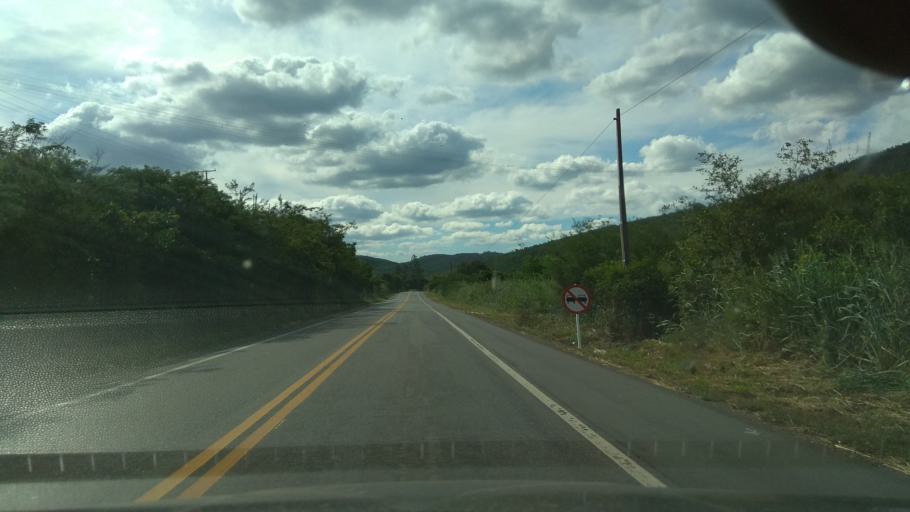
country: BR
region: Bahia
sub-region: Jequie
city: Jequie
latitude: -13.9072
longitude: -40.0174
